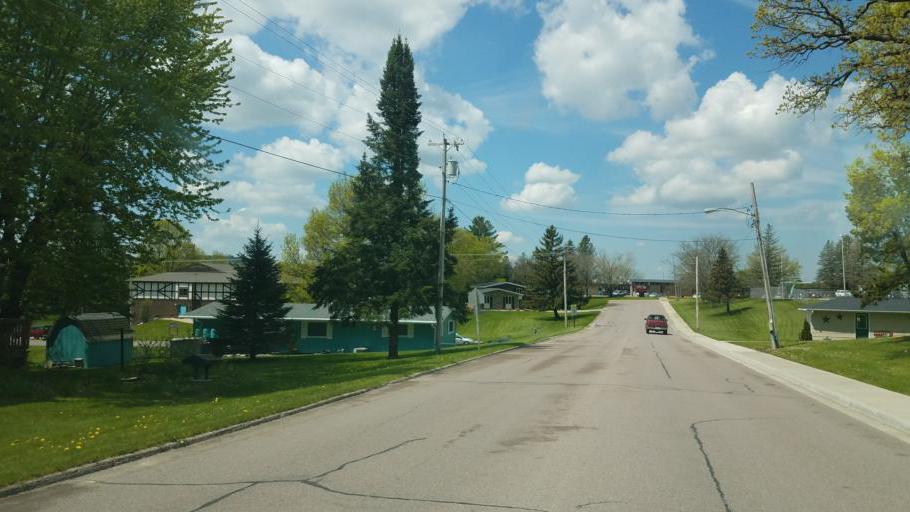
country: US
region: Wisconsin
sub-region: Vernon County
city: Hillsboro
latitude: 43.6563
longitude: -90.3487
